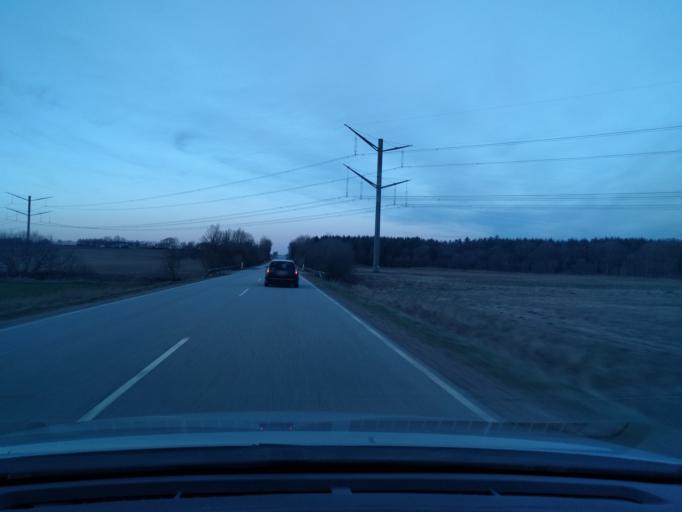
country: DK
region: South Denmark
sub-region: Vejen Kommune
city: Rodding
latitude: 55.3402
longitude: 9.1662
